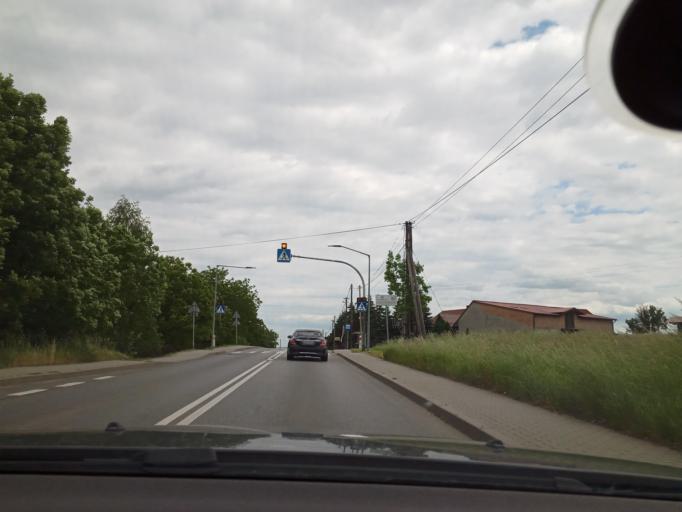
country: PL
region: Lesser Poland Voivodeship
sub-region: Powiat wielicki
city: Trabki
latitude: 49.9726
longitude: 20.1227
